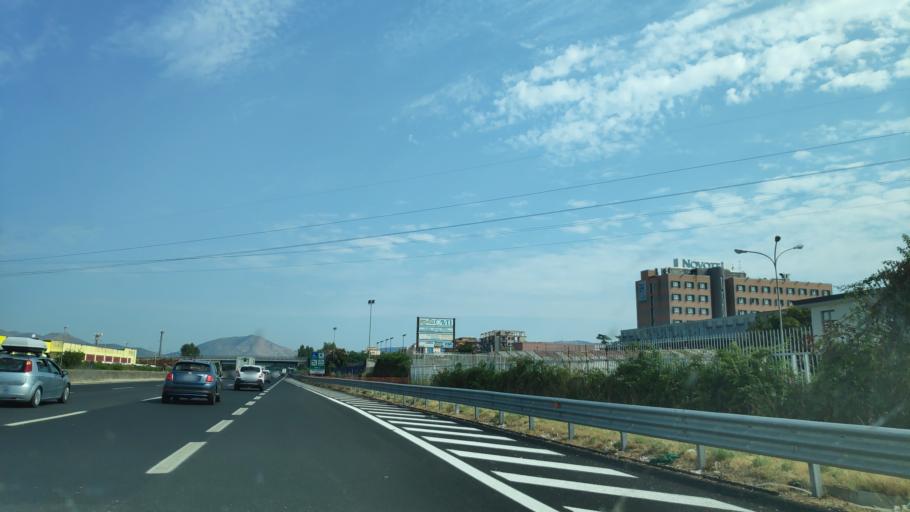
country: IT
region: Campania
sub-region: Provincia di Caserta
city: Capodrise
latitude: 41.0407
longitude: 14.3227
